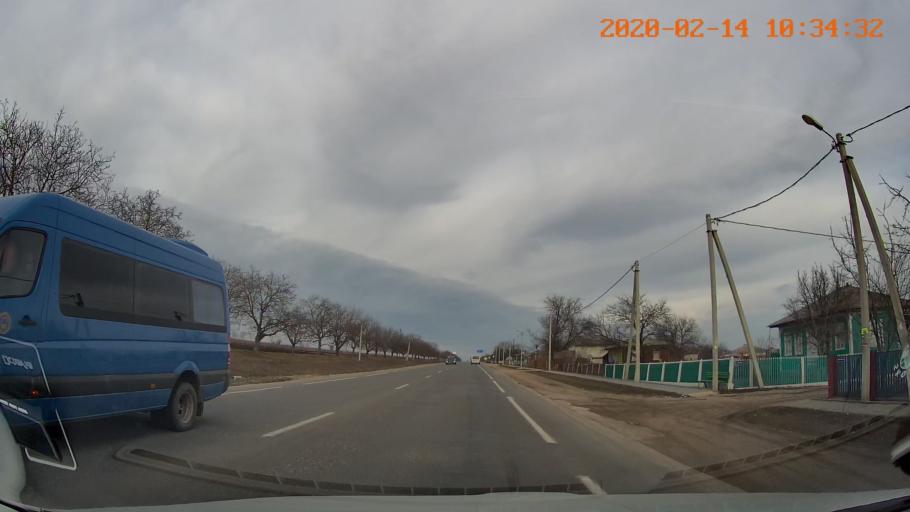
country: MD
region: Riscani
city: Riscani
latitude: 47.9044
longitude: 27.6644
